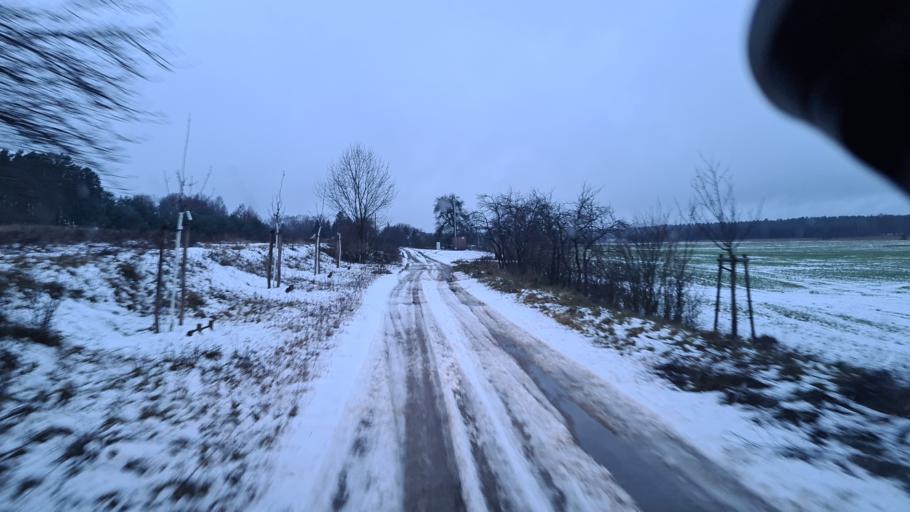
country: DE
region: Brandenburg
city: Schenkendobern
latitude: 51.9038
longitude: 14.5854
